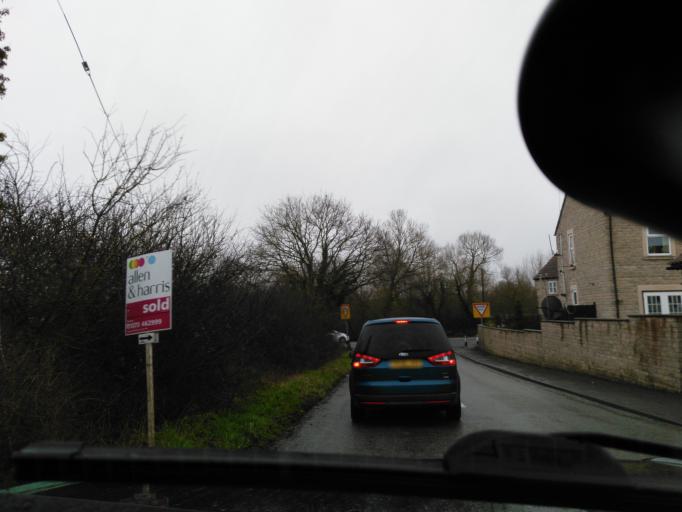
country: GB
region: England
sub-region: Wiltshire
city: Wingfield
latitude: 51.2827
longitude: -2.2733
